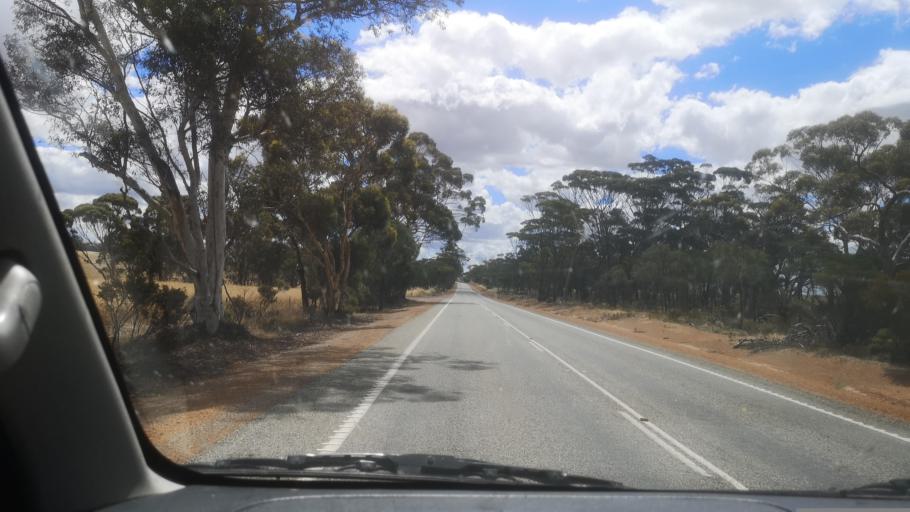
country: AU
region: Western Australia
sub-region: Beverley
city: Beverley
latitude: -32.0055
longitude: 117.1899
